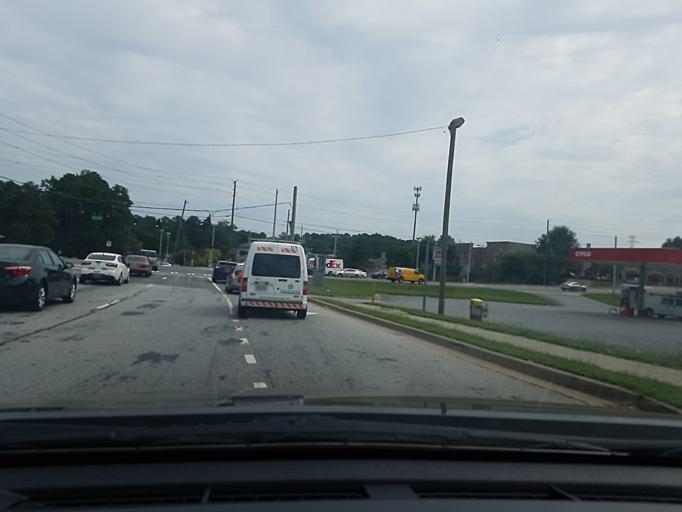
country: US
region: Georgia
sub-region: Gwinnett County
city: Norcross
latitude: 33.9498
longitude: -84.1988
